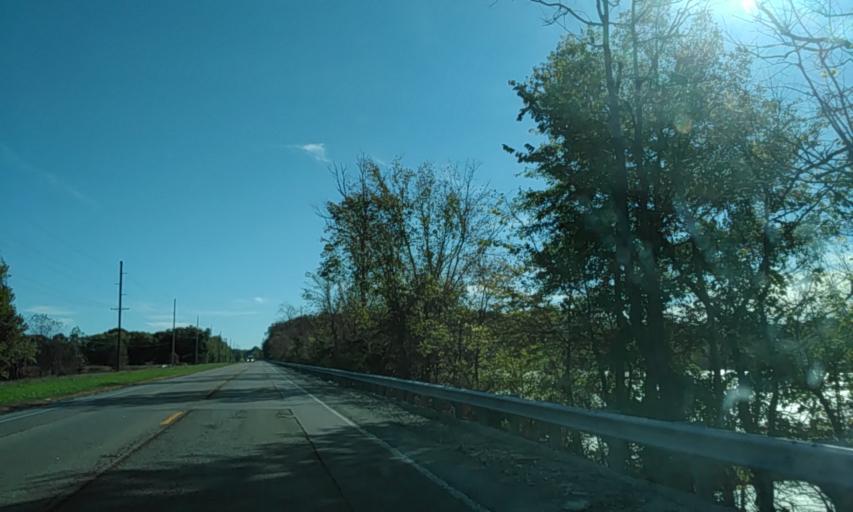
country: US
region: Illinois
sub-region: Madison County
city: Troy
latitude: 38.7169
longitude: -89.8354
